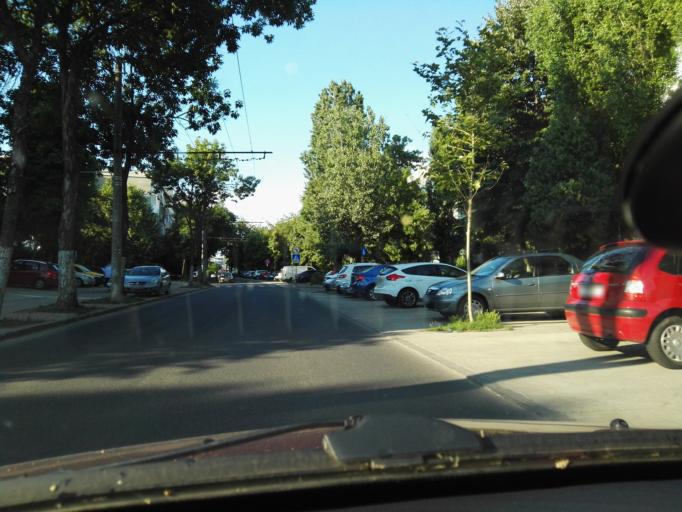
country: RO
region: Bucuresti
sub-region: Municipiul Bucuresti
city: Bucuresti
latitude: 44.3865
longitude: 26.1032
